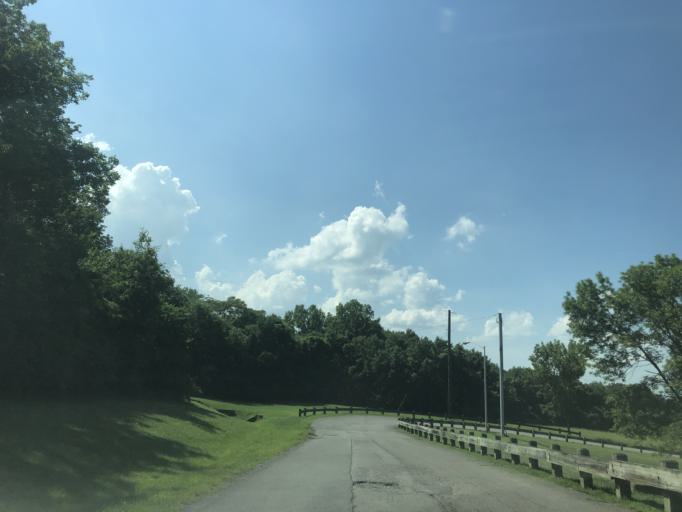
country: US
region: Tennessee
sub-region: Davidson County
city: Lakewood
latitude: 36.1546
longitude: -86.6238
